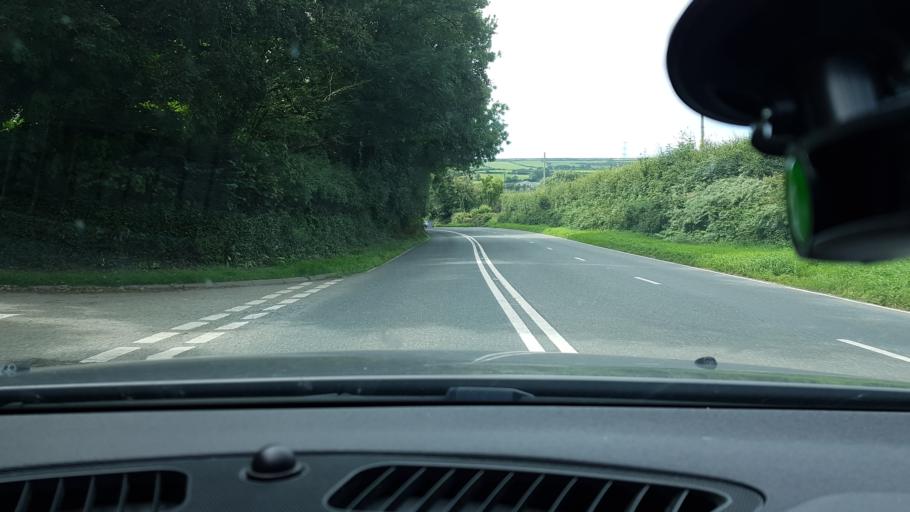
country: GB
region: England
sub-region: Cornwall
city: Camelford
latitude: 50.5951
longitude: -4.7188
